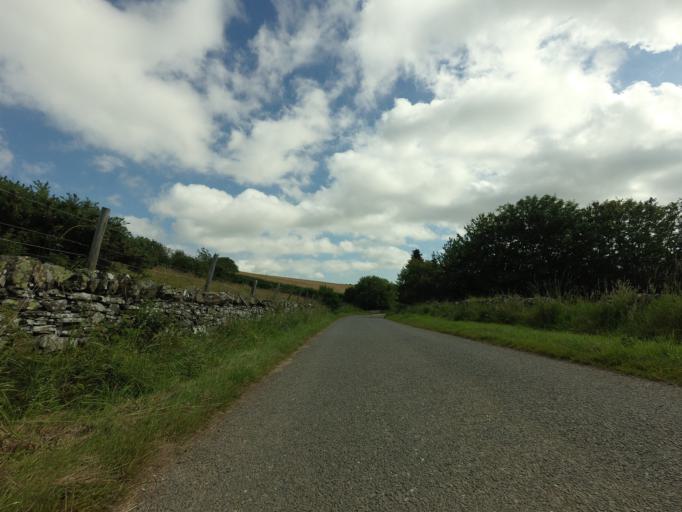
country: GB
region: Scotland
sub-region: Aberdeenshire
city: Banff
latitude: 57.6010
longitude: -2.5116
